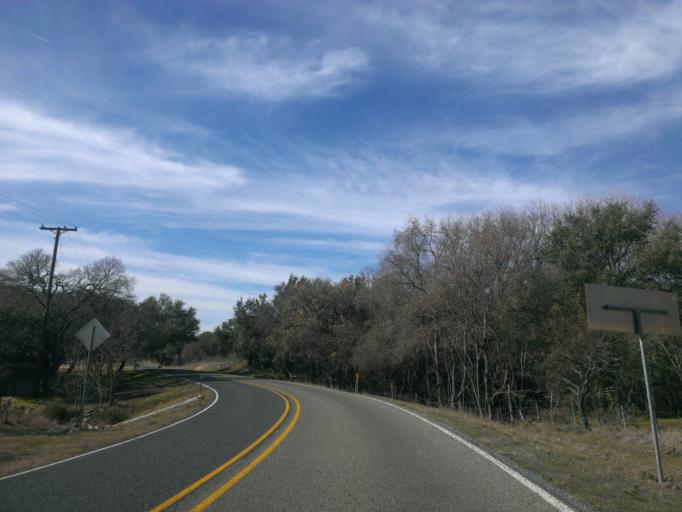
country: US
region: Texas
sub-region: Burnet County
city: Granite Shoals
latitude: 30.6042
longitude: -98.4174
